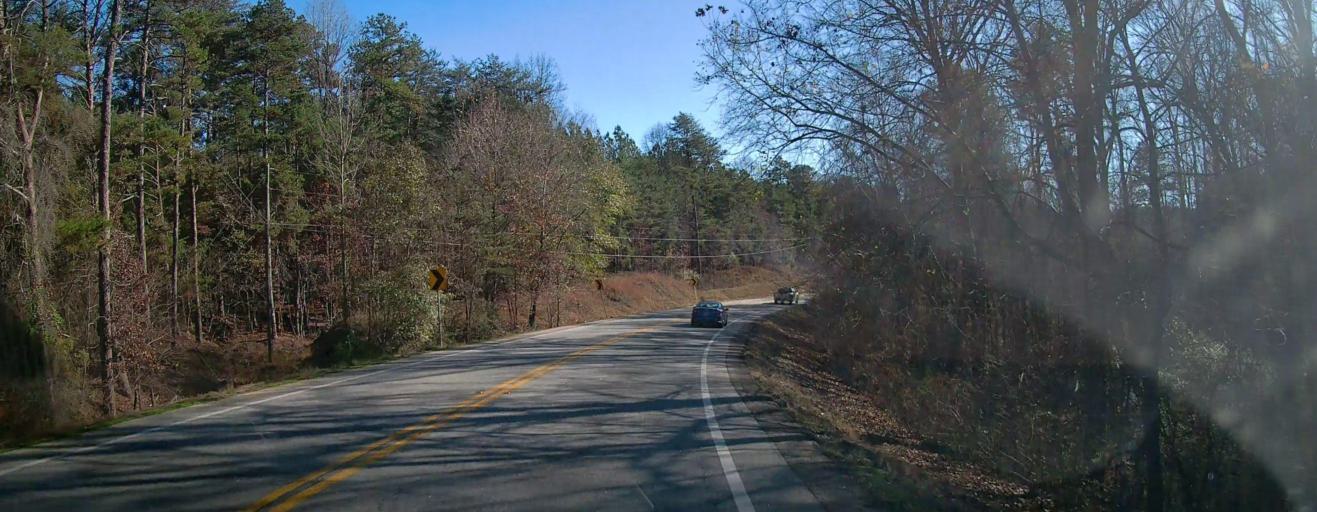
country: US
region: Georgia
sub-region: Hall County
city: Lula
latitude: 34.4195
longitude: -83.7075
